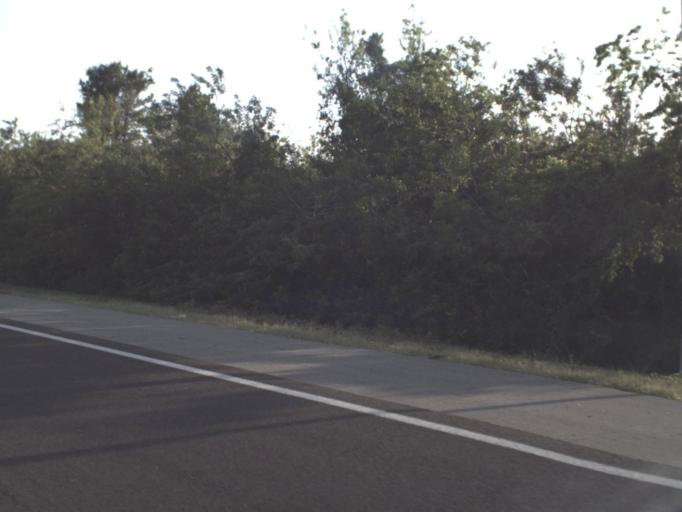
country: US
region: Florida
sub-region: Brevard County
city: Titusville
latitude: 28.6099
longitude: -80.8514
